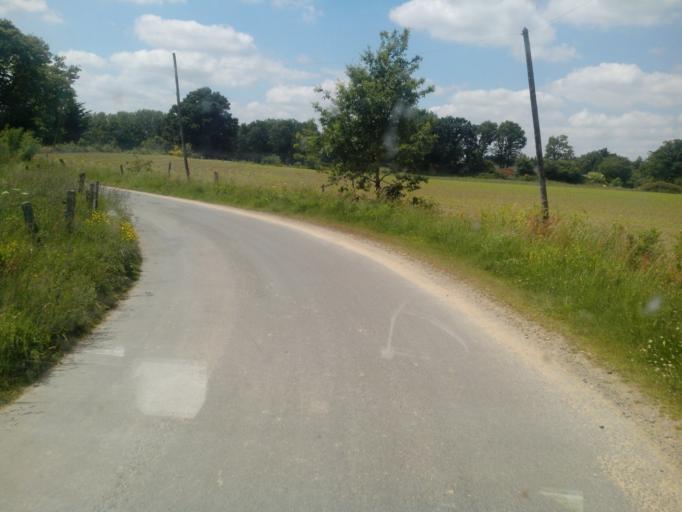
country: FR
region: Brittany
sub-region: Departement d'Ille-et-Vilaine
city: Saint-Marc-le-Blanc
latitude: 48.3504
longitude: -1.4169
